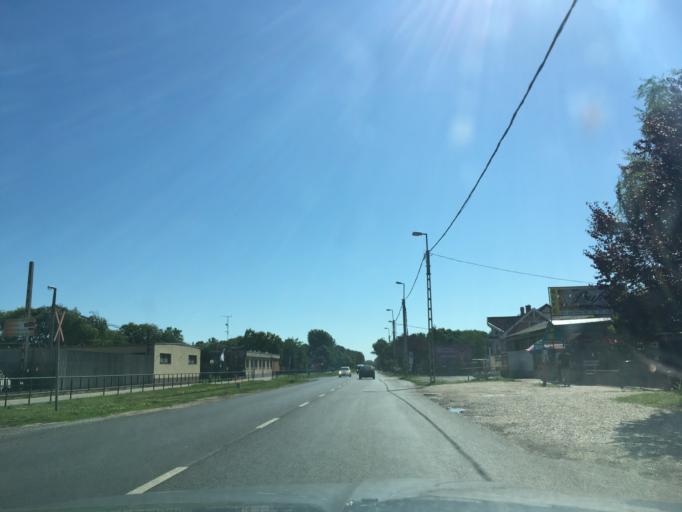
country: HU
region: Hajdu-Bihar
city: Debrecen
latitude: 47.5310
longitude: 21.6806
